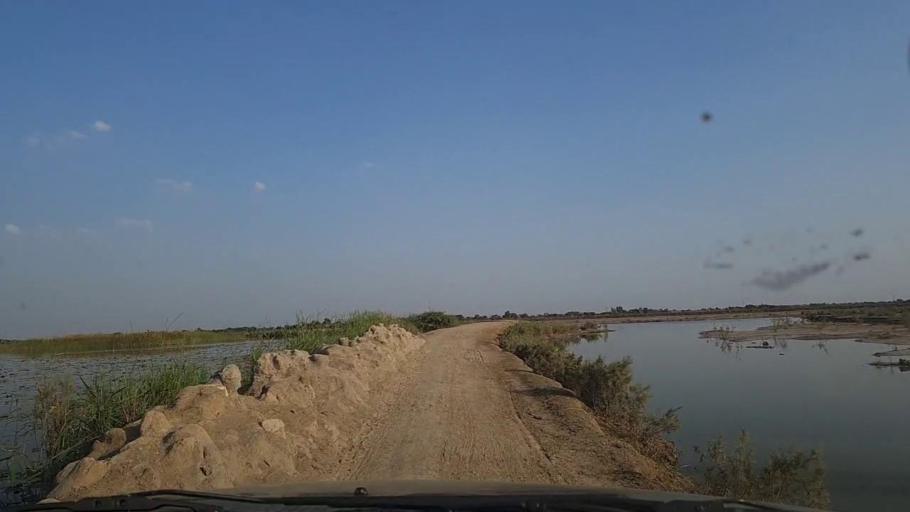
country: PK
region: Sindh
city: Daro Mehar
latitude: 24.7507
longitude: 68.0832
